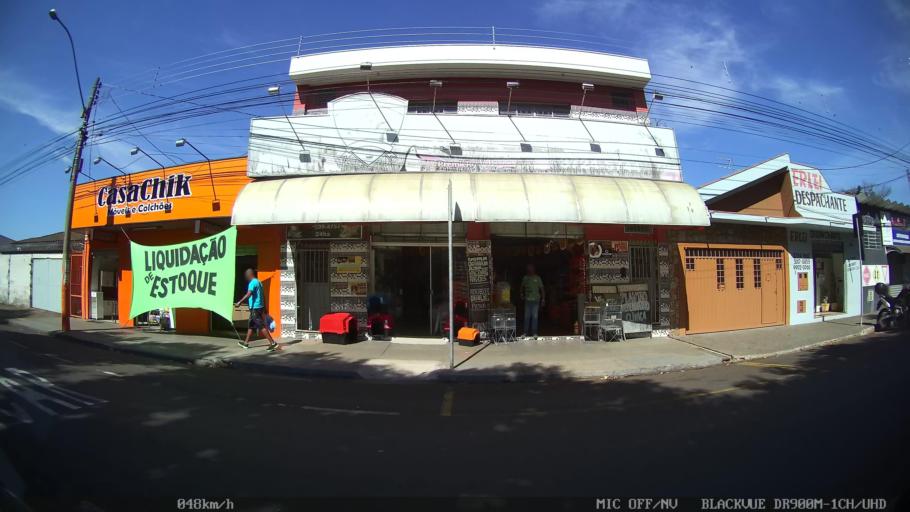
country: BR
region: Sao Paulo
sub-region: Franca
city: Franca
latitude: -20.5153
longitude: -47.4067
